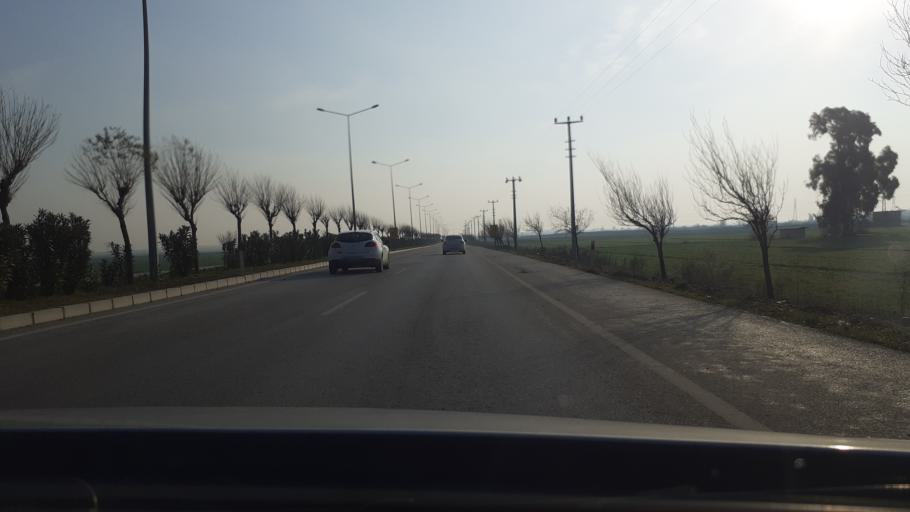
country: TR
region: Hatay
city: Serinyol
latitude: 36.3717
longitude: 36.2353
